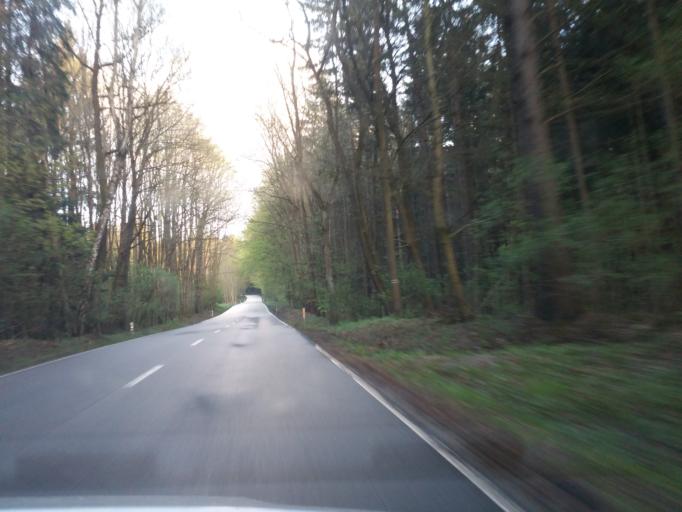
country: CZ
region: South Moravian
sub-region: Okres Blansko
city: Boskovice
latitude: 49.4759
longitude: 16.6989
